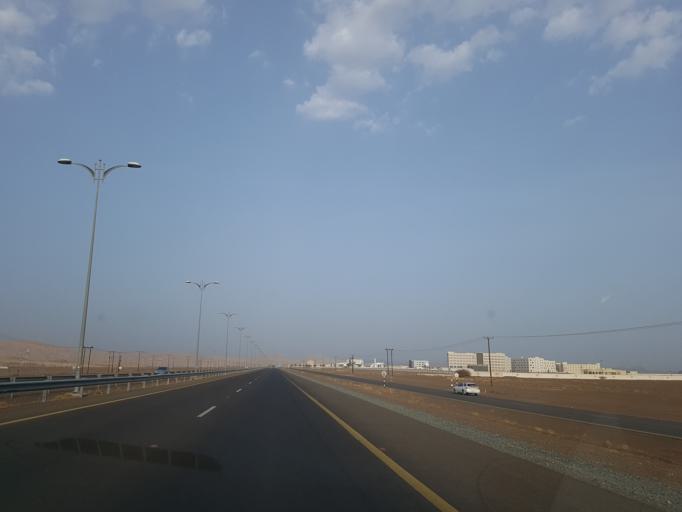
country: OM
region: Al Buraimi
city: Al Buraymi
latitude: 24.2382
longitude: 55.8838
